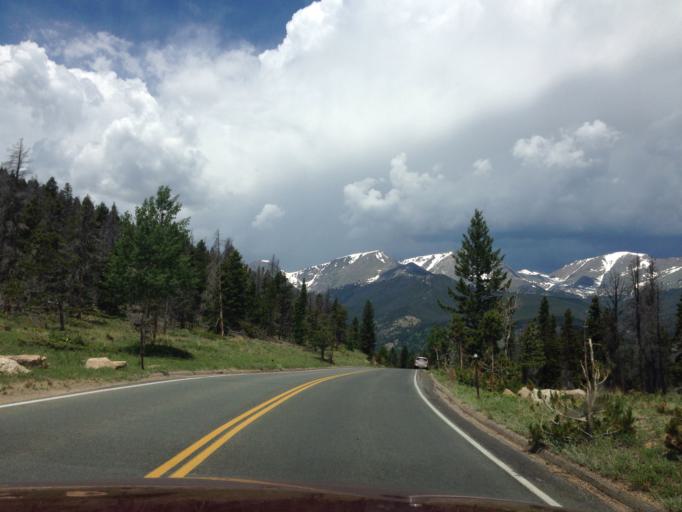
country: US
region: Colorado
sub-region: Larimer County
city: Estes Park
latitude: 40.3892
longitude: -105.6185
